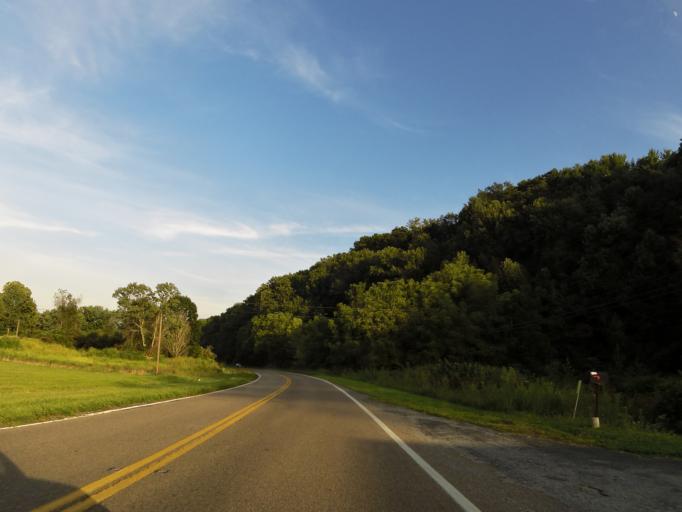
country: US
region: Virginia
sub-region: Washington County
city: Emory
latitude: 36.6438
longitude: -81.8241
